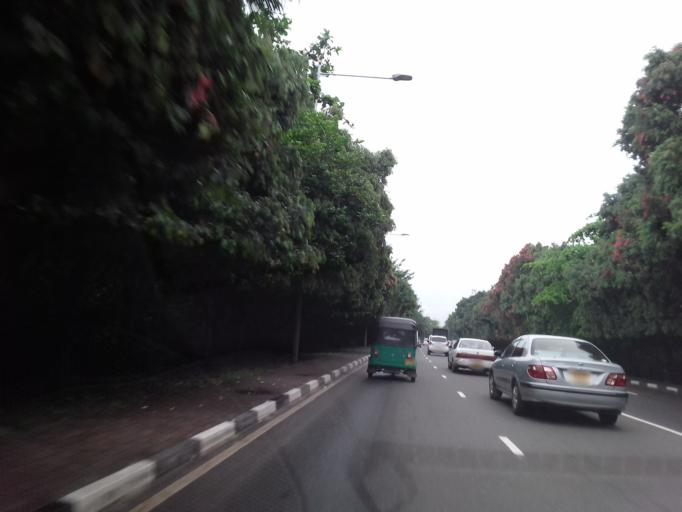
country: LK
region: Western
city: Battaramulla South
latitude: 6.8966
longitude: 79.9146
